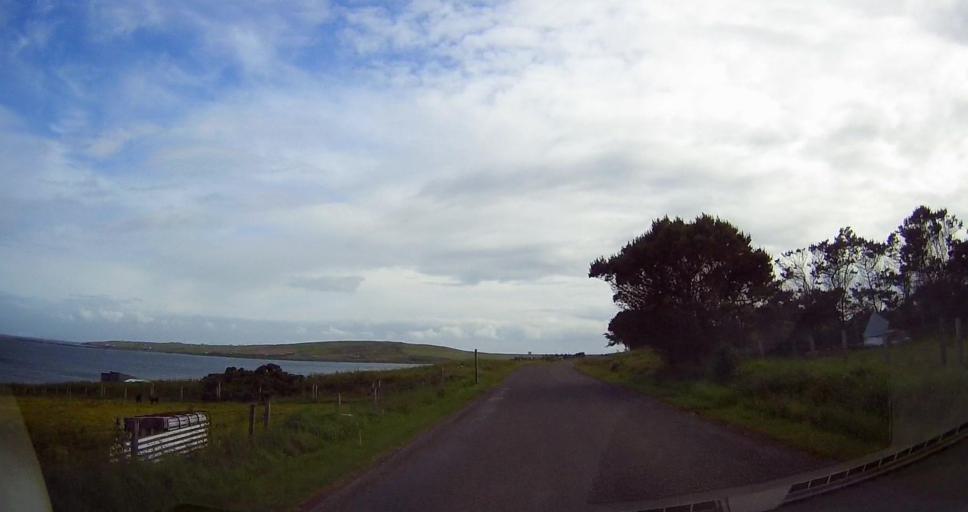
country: GB
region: Scotland
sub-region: Orkney Islands
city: Stromness
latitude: 58.7980
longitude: -3.2521
